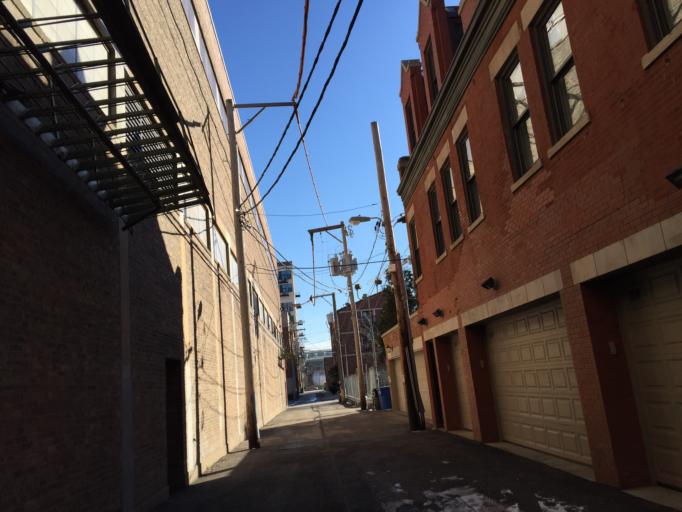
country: US
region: Illinois
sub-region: Cook County
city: Chicago
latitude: 41.8563
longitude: -87.6198
